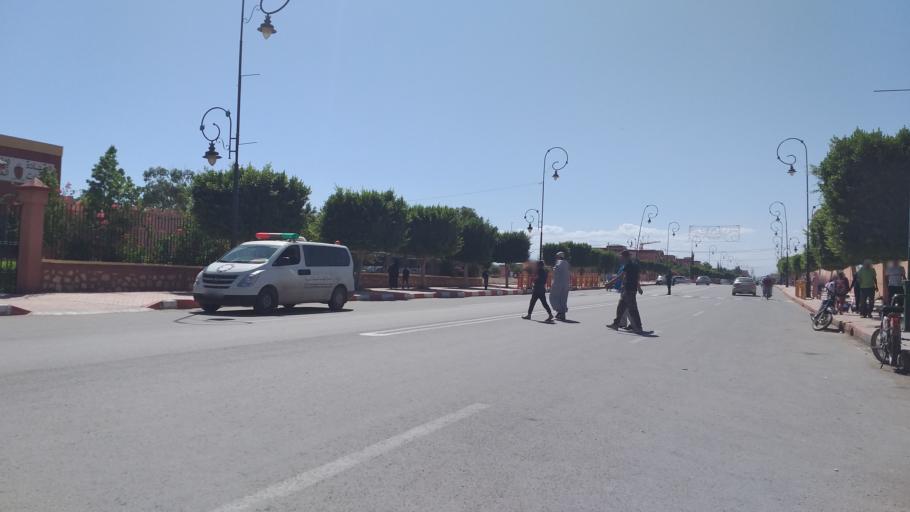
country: MA
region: Marrakech-Tensift-Al Haouz
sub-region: Chichaoua
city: Chichaoua
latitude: 31.5416
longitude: -8.7671
